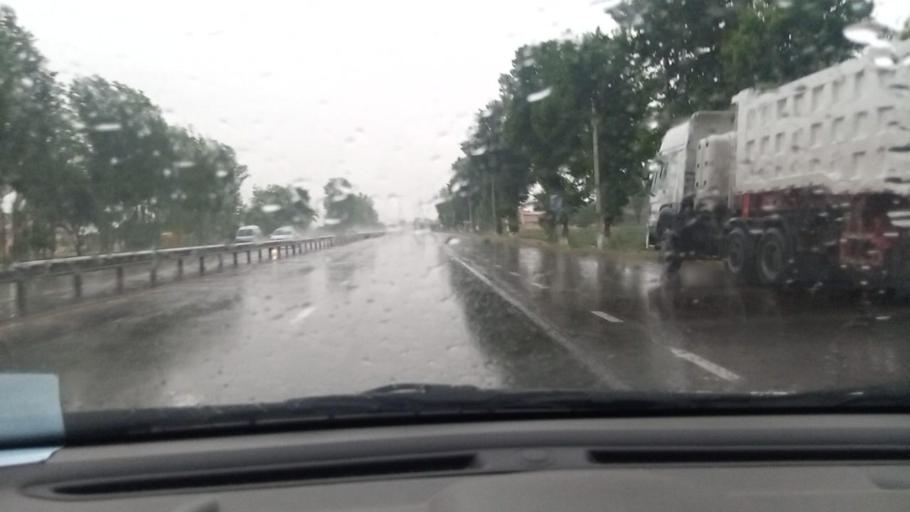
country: UZ
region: Toshkent Shahri
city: Bektemir
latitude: 41.1569
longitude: 69.4232
